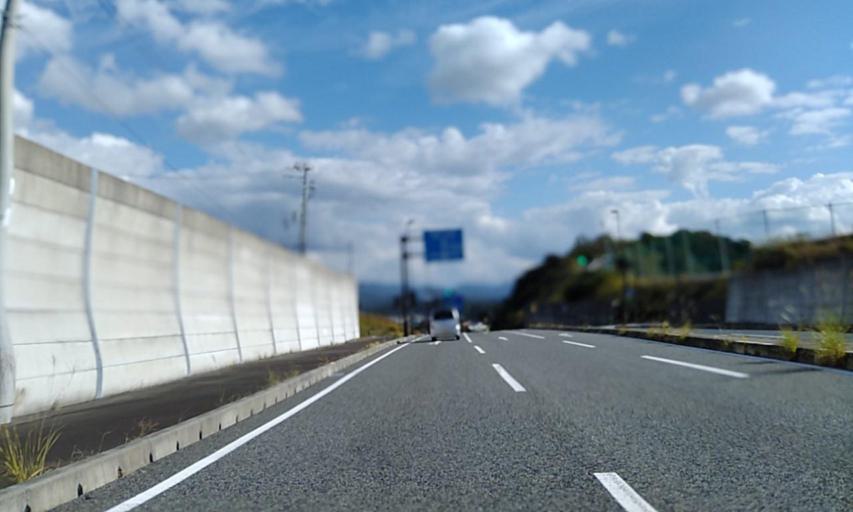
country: JP
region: Wakayama
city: Tanabe
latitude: 33.7474
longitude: 135.3652
